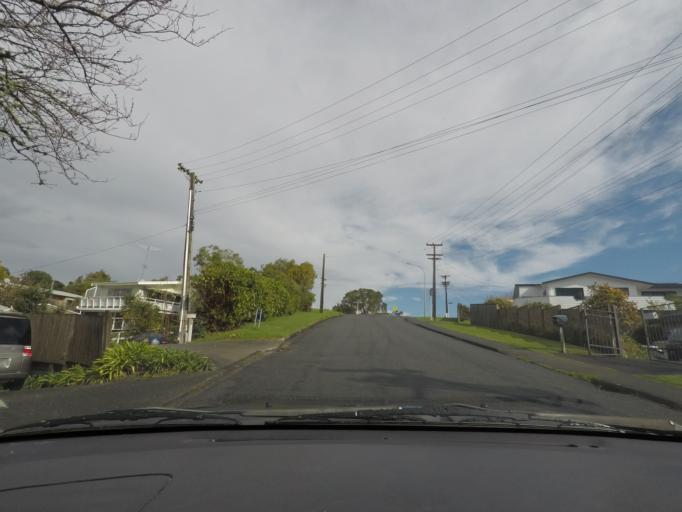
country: NZ
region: Auckland
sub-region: Auckland
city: Warkworth
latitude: -36.4232
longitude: 174.7306
